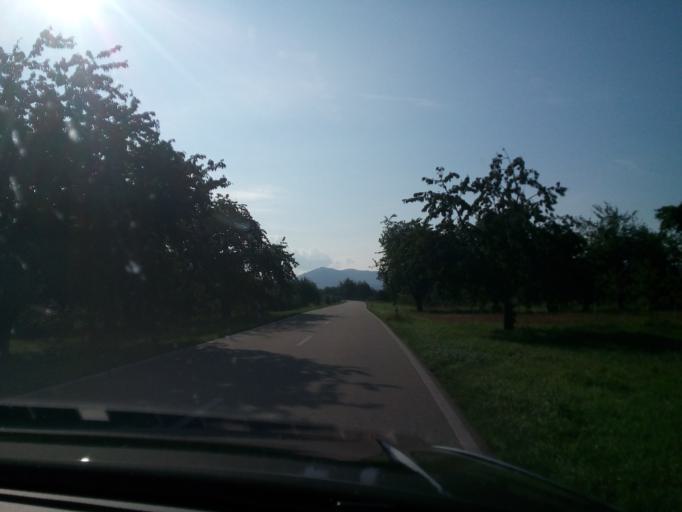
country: DE
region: Baden-Wuerttemberg
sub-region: Freiburg Region
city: Haslach
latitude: 48.5553
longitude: 8.0513
